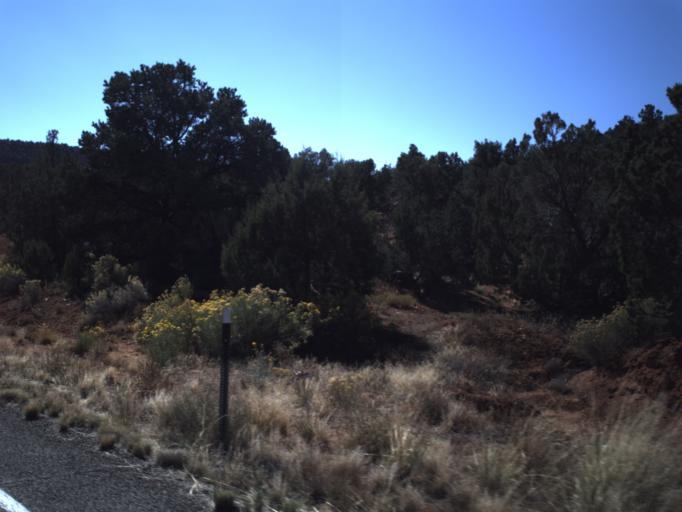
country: US
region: Utah
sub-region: San Juan County
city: Blanding
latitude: 37.5712
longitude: -110.0369
